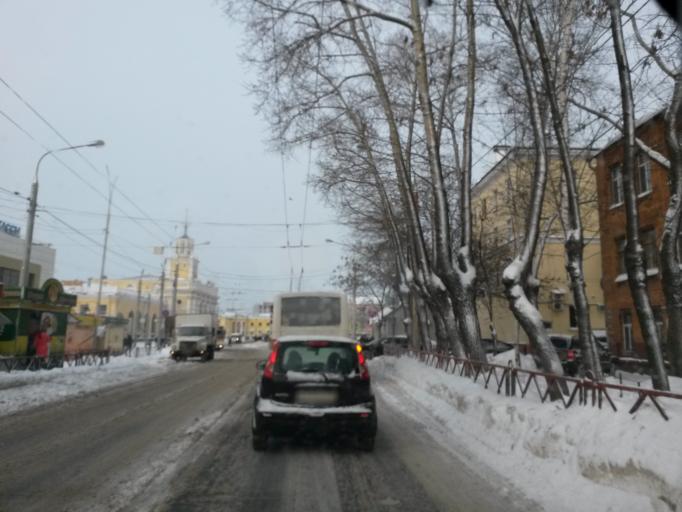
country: RU
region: Jaroslavl
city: Yaroslavl
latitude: 57.6252
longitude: 39.8380
